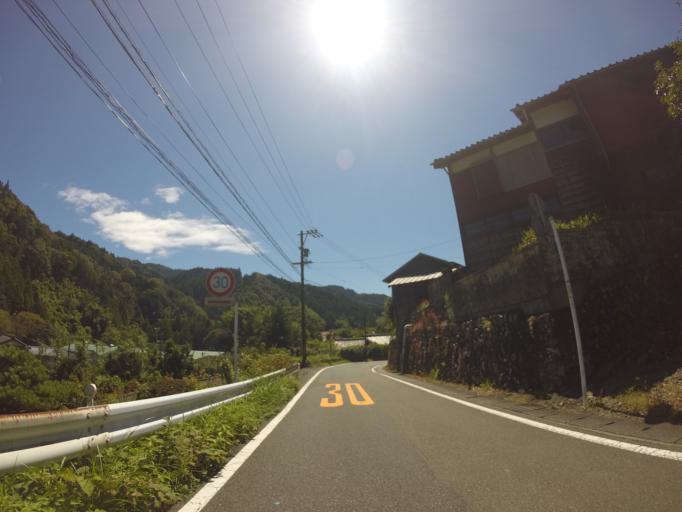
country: JP
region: Shizuoka
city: Fujieda
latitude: 34.9687
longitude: 138.2124
